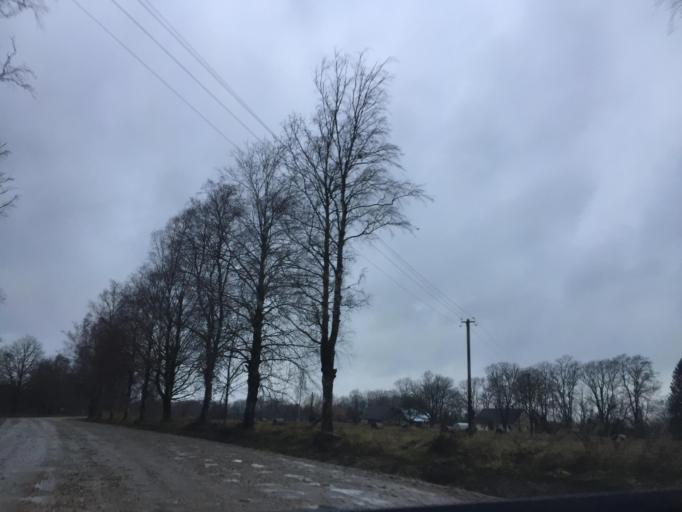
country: LV
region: Salacgrivas
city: Salacgriva
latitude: 57.7500
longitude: 24.4106
